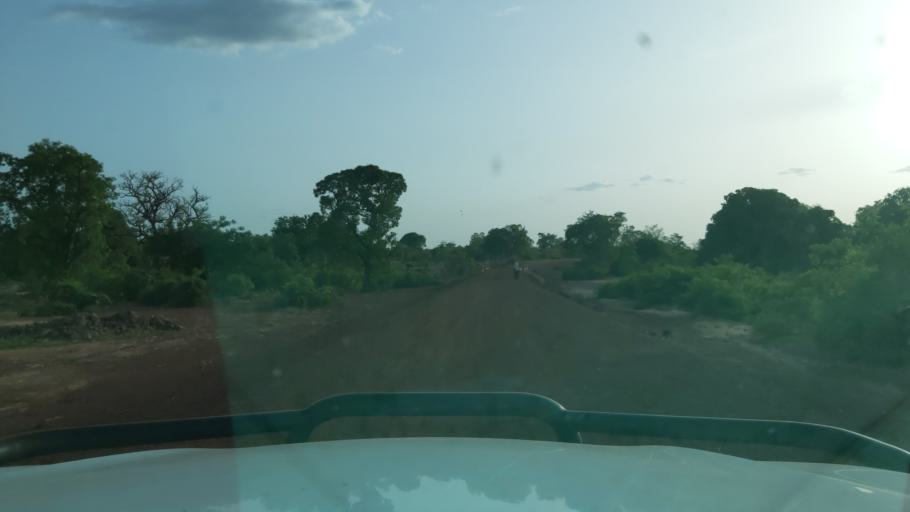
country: ML
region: Koulikoro
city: Kolokani
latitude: 13.2052
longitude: -7.9194
